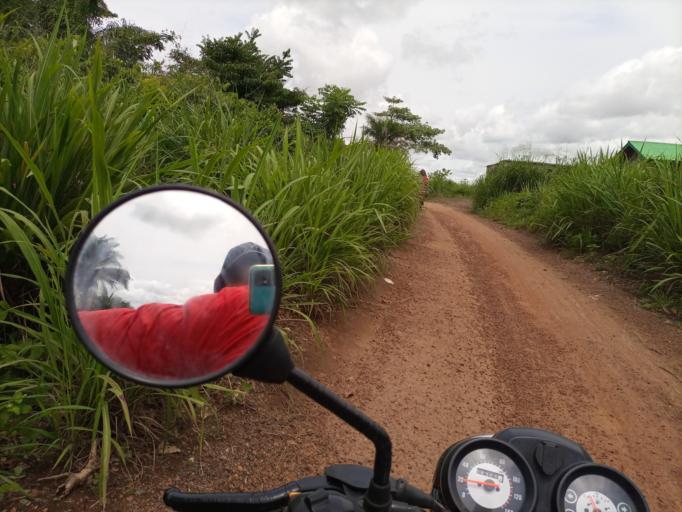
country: SL
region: Southern Province
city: Baoma
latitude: 7.9792
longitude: -11.7124
